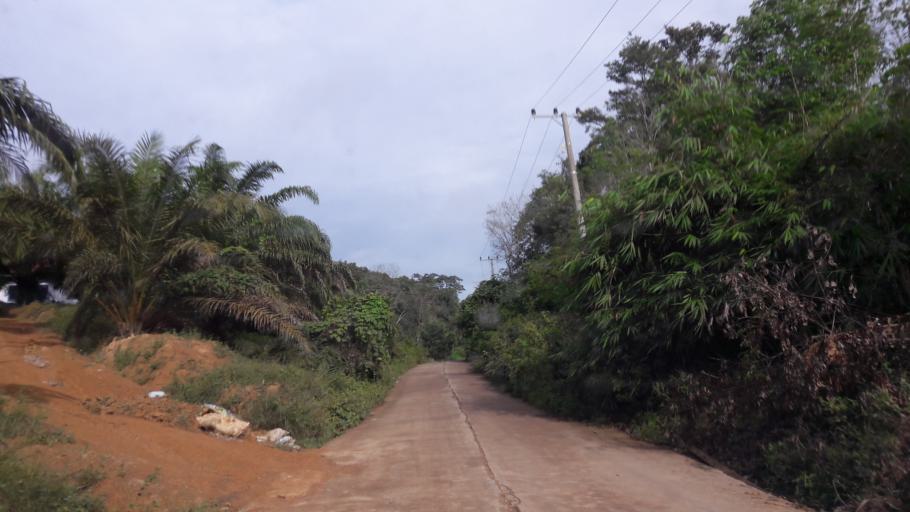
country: ID
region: South Sumatra
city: Gunungmegang Dalam
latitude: -3.2820
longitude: 103.7568
